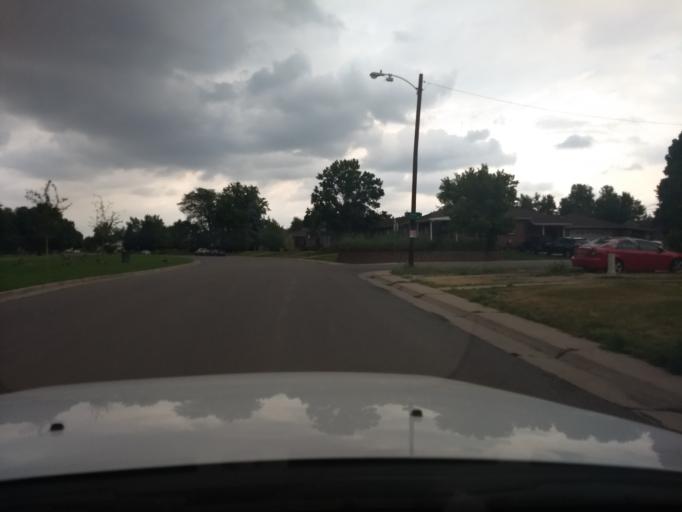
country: US
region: Colorado
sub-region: Denver County
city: Denver
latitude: 39.7008
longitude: -105.0138
